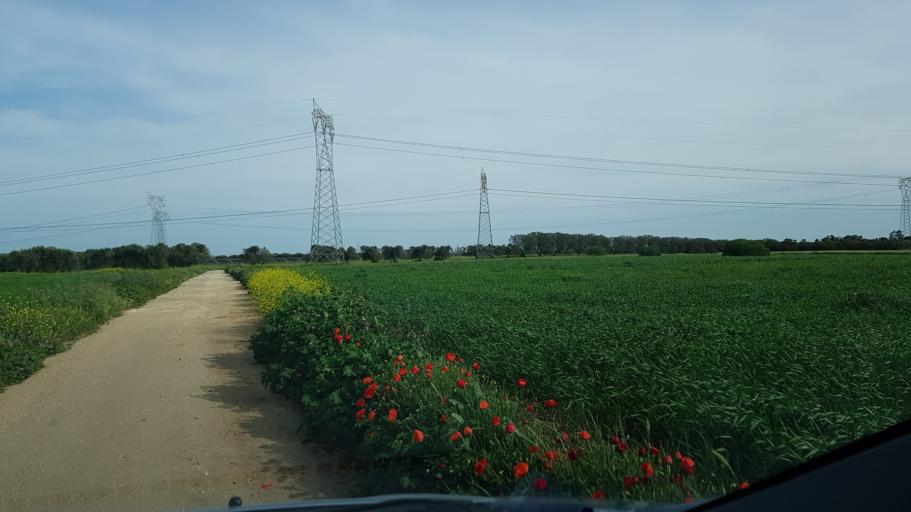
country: IT
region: Apulia
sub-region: Provincia di Brindisi
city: Tuturano
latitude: 40.5555
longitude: 17.9261
